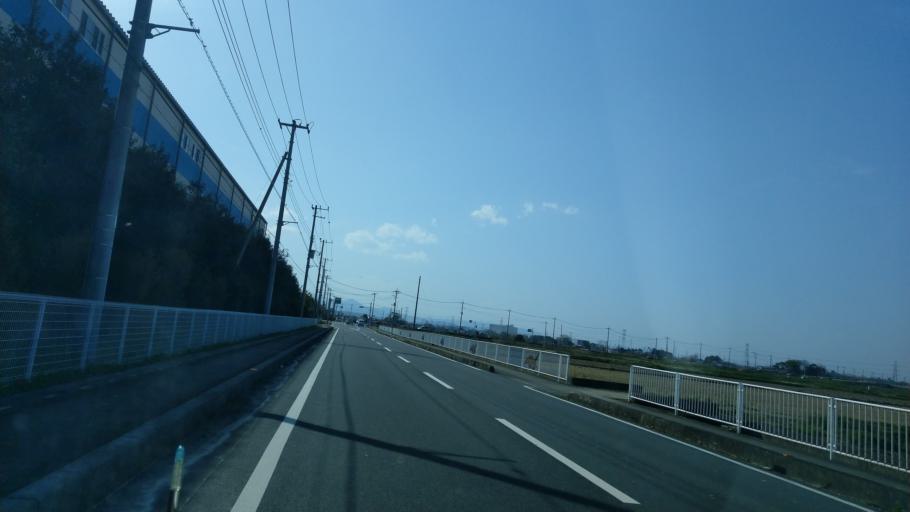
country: JP
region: Saitama
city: Sakado
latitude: 35.9882
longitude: 139.4624
